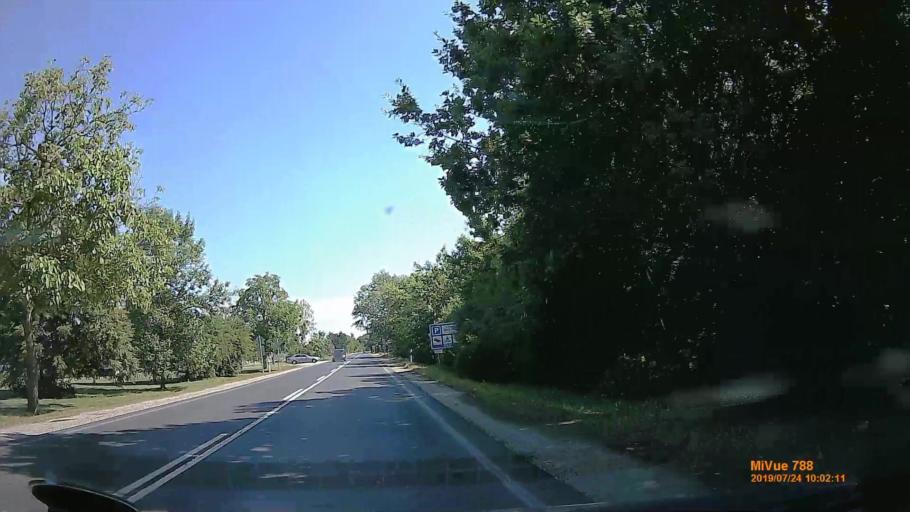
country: HU
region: Szabolcs-Szatmar-Bereg
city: Vasarosnameny
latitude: 48.1088
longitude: 22.3042
